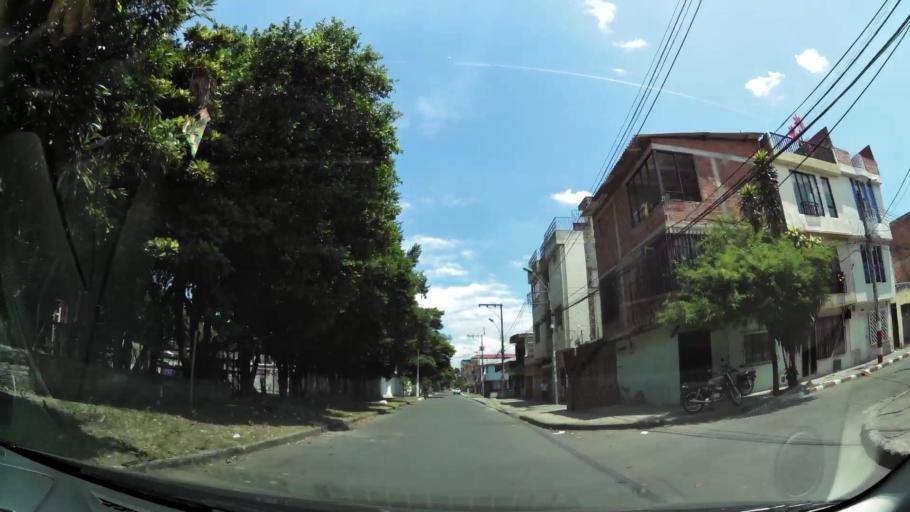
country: CO
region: Valle del Cauca
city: Cali
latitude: 3.4459
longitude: -76.5014
